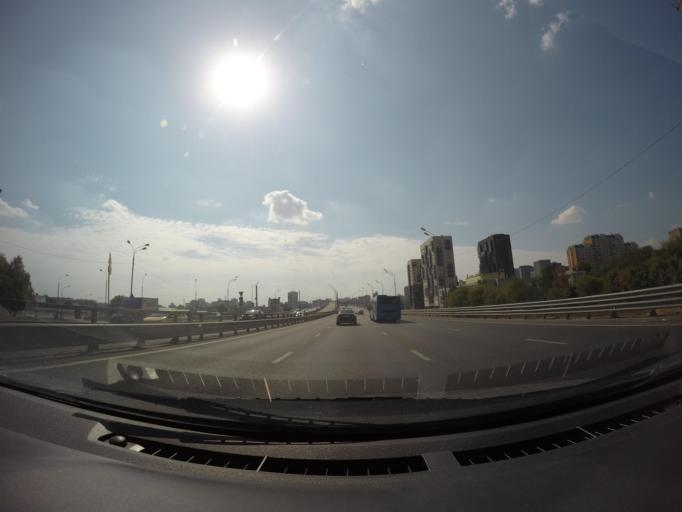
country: RU
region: Moscow
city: Zapadnoye Degunino
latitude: 55.8711
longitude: 37.5180
